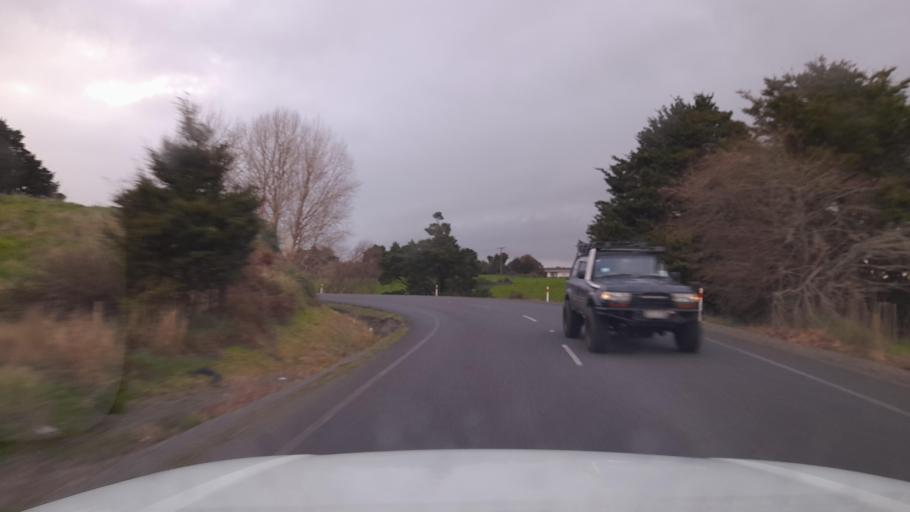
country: NZ
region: Northland
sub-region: Whangarei
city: Maungatapere
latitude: -35.6964
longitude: 174.1844
